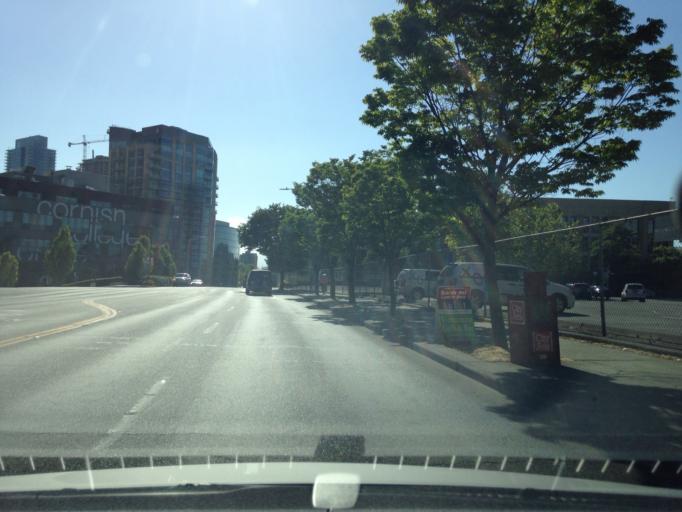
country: US
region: Washington
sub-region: King County
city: Seattle
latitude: 47.6186
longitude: -122.3345
